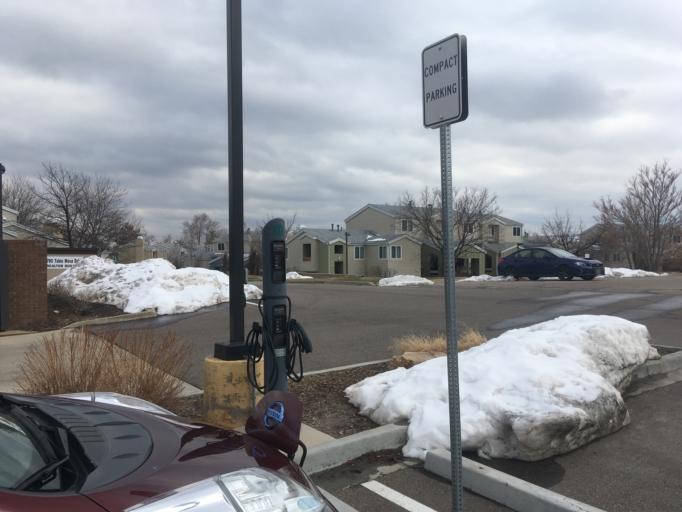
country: US
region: Colorado
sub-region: Boulder County
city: Boulder
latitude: 39.9852
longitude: -105.2374
